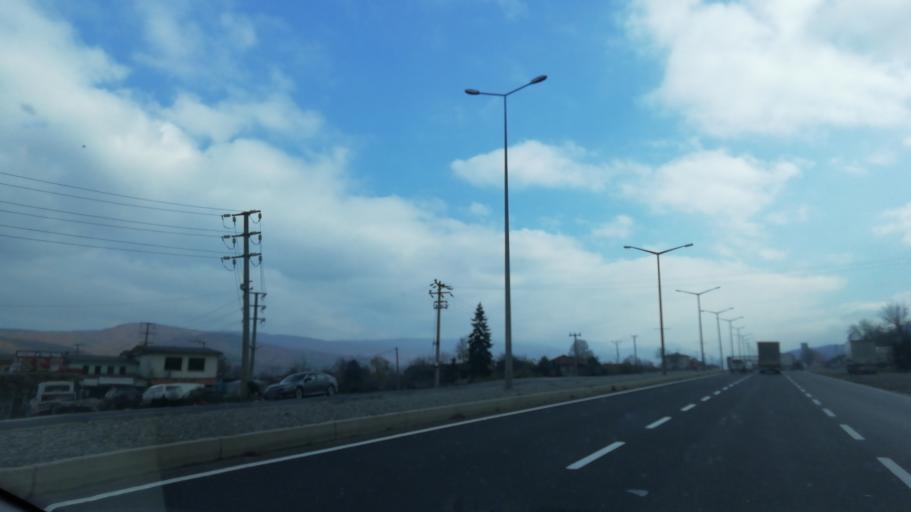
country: TR
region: Duzce
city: Kaynasli
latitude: 40.7772
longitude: 31.2975
